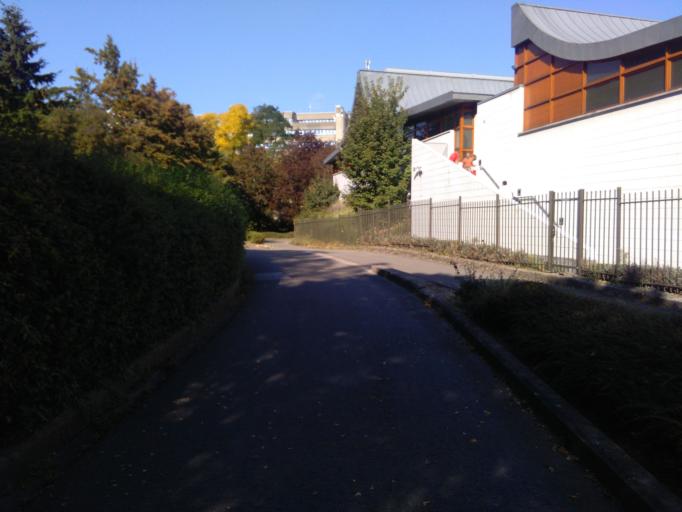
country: BE
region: Brussels Capital
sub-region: Bruxelles-Capitale
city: Brussels
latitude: 50.8204
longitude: 4.3985
